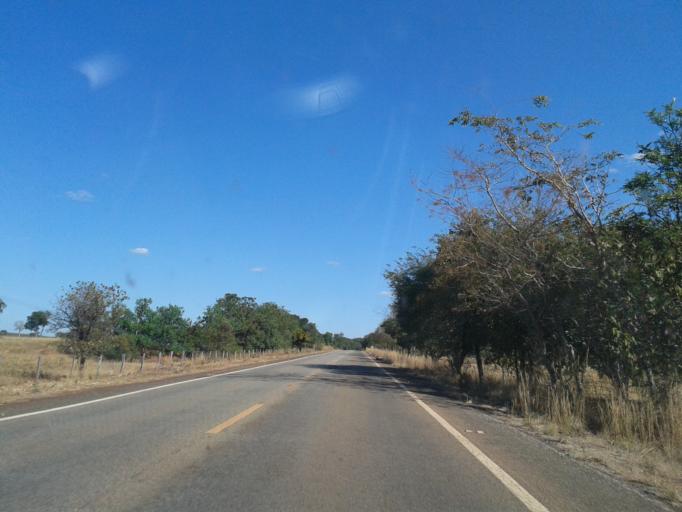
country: BR
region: Goias
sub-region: Mozarlandia
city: Mozarlandia
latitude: -14.3022
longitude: -50.4039
